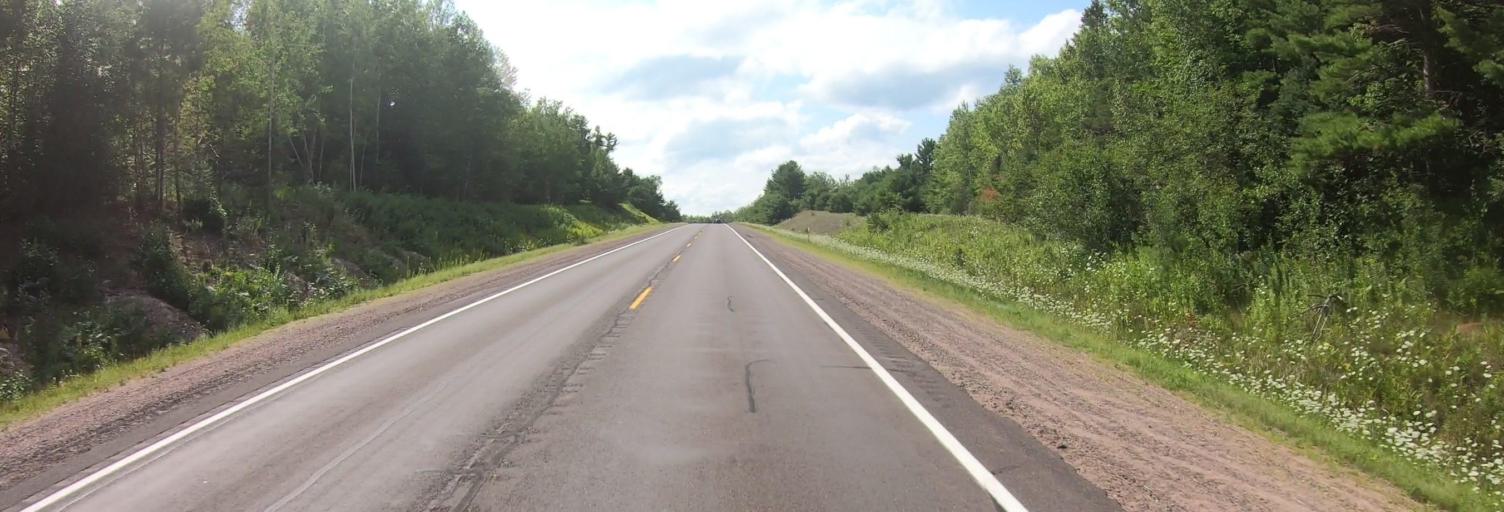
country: US
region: Michigan
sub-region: Ontonagon County
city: Ontonagon
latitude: 46.5338
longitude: -89.2075
